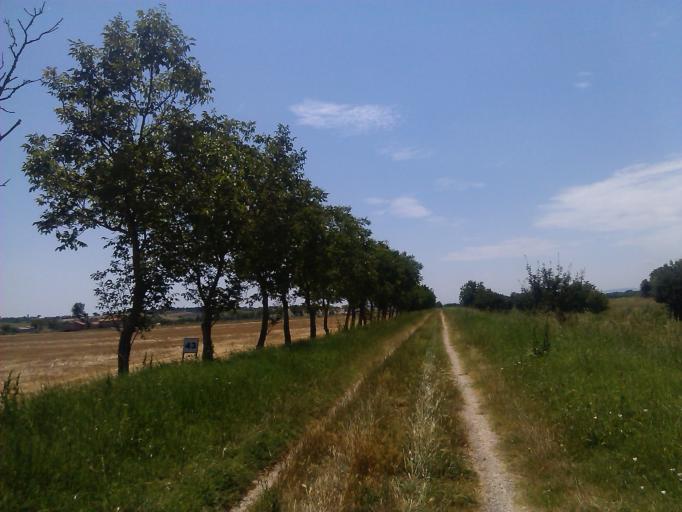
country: IT
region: Tuscany
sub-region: Province of Arezzo
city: Cesa
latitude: 43.3082
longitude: 11.8390
